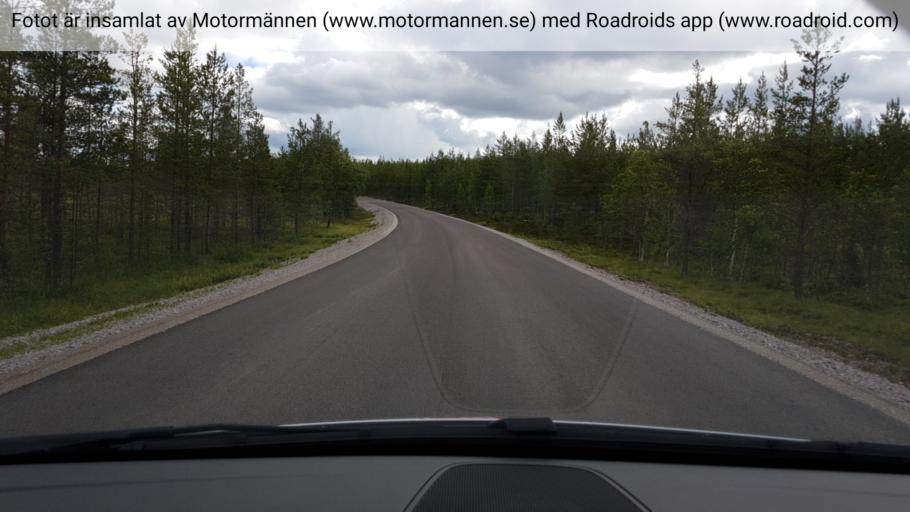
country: SE
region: Jaemtland
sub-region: Harjedalens Kommun
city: Sveg
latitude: 61.7108
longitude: 14.1696
